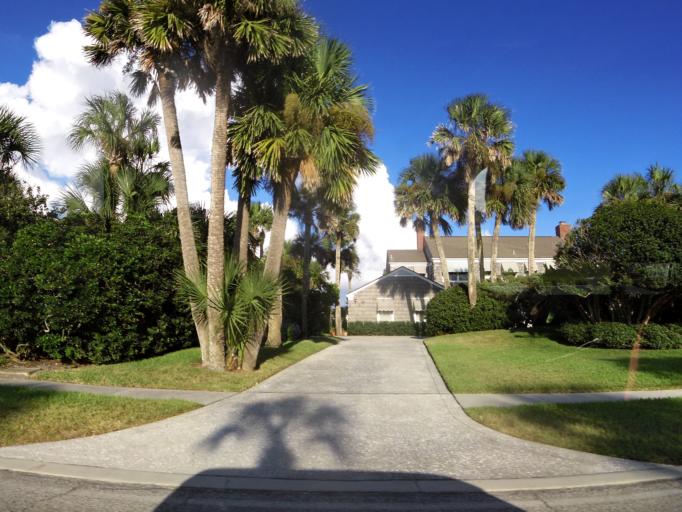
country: US
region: Florida
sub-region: Saint Johns County
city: Ponte Vedra Beach
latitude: 30.2462
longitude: -81.3799
